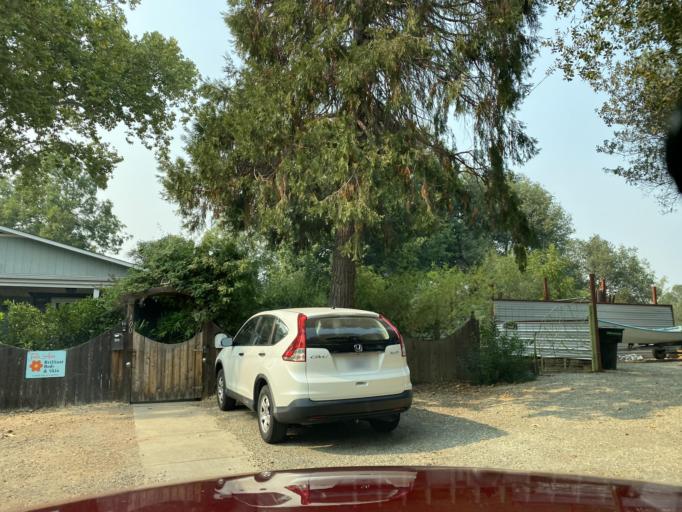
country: US
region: California
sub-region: Sacramento County
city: Folsom
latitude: 38.6799
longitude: -121.1705
